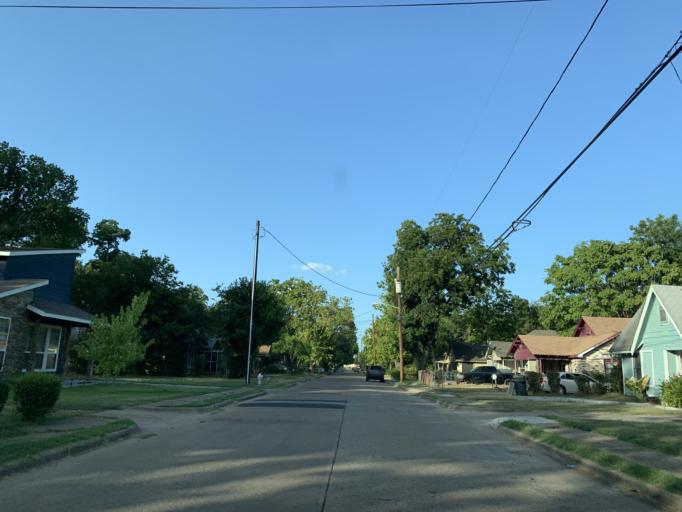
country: US
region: Texas
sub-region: Dallas County
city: Dallas
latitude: 32.7541
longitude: -96.7570
